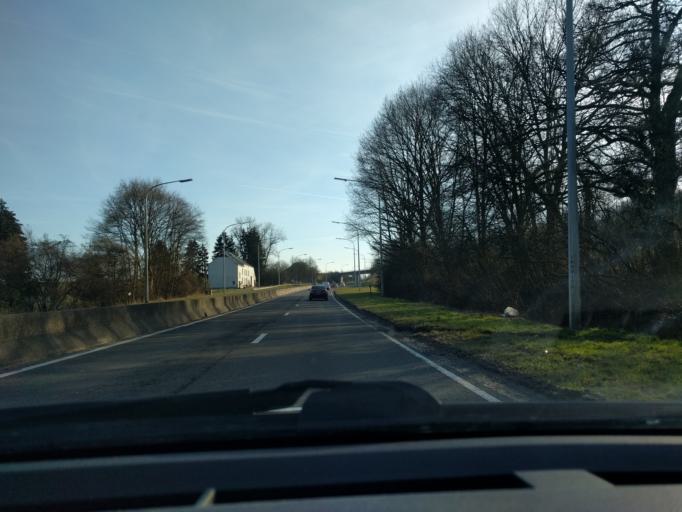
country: BE
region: Wallonia
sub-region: Province de Namur
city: Philippeville
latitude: 50.1418
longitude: 4.5041
